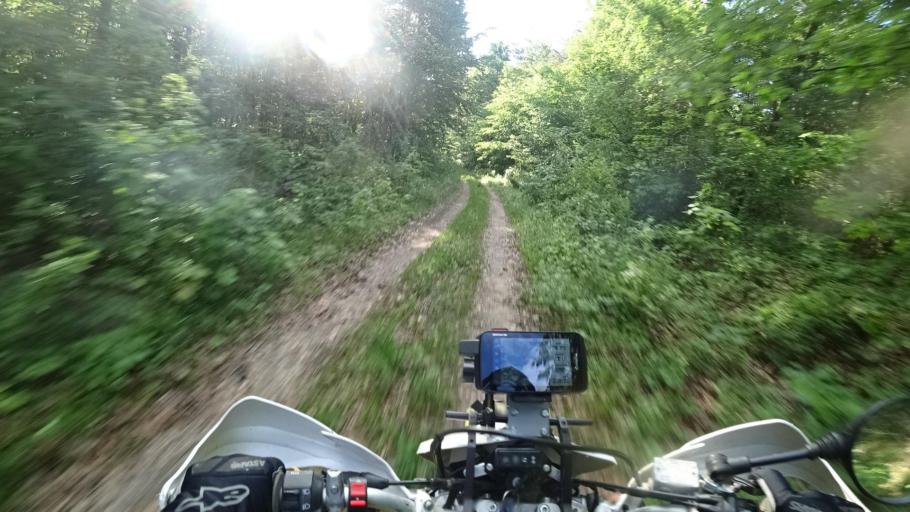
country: BA
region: Federation of Bosnia and Herzegovina
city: Sanica
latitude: 44.6555
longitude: 16.6110
